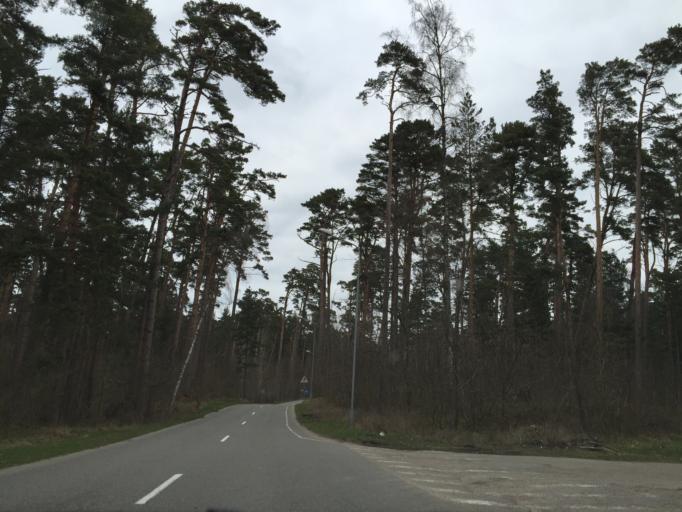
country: LT
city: Nida
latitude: 55.3148
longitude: 21.0113
